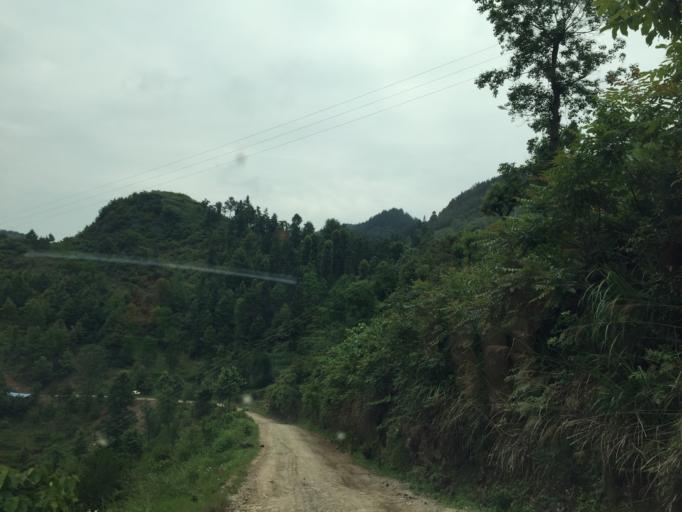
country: CN
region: Guizhou Sheng
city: Tongjing
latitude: 28.3713
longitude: 108.2380
